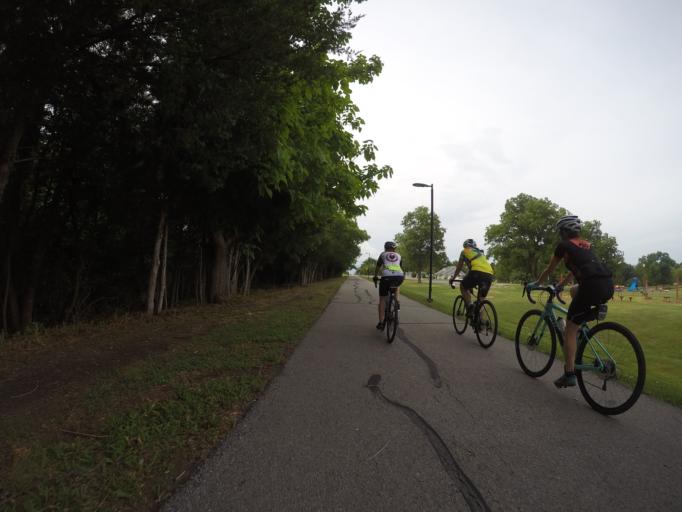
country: US
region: Kansas
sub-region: Franklin County
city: Ottawa
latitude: 38.5984
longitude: -95.2703
